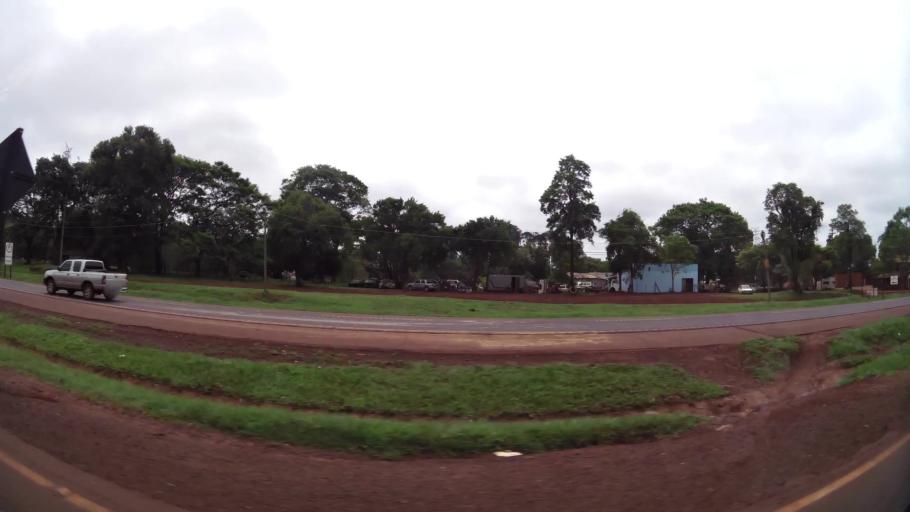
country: PY
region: Alto Parana
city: Ciudad del Este
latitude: -25.4934
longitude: -54.7201
